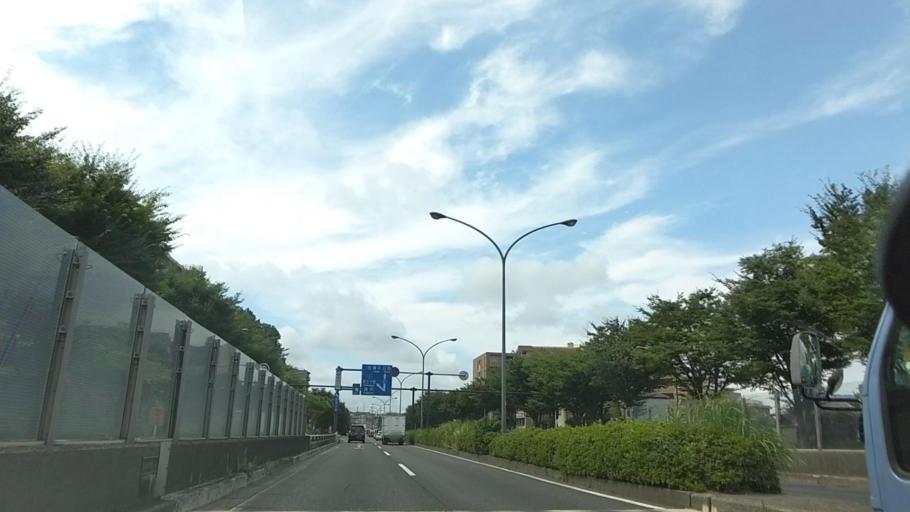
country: JP
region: Kanagawa
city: Yokohama
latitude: 35.4247
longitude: 139.5612
